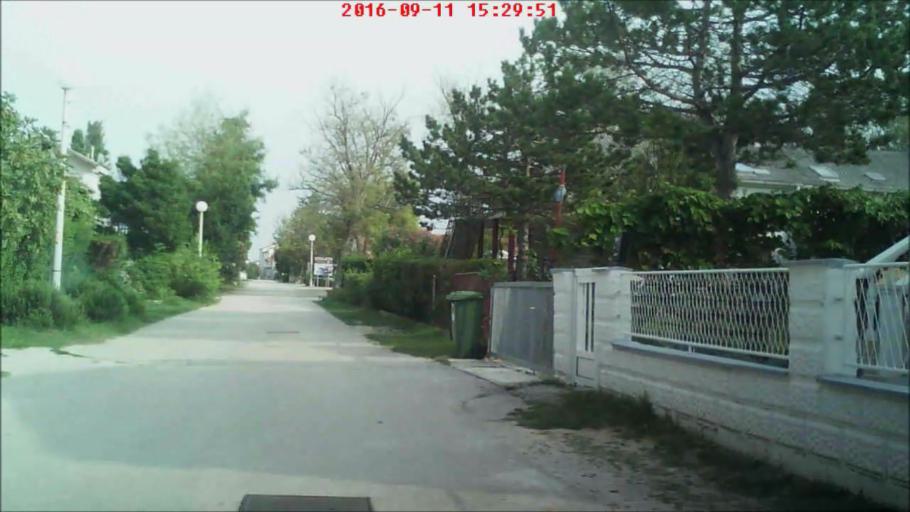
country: HR
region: Zadarska
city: Nin
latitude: 44.2591
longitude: 15.1599
